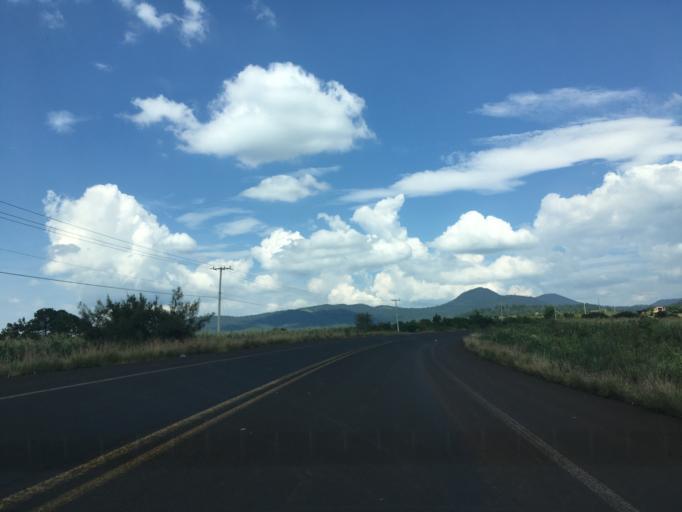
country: MX
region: Michoacan
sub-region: Tingueindin
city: Tingueindin
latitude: 19.8372
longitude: -102.4924
